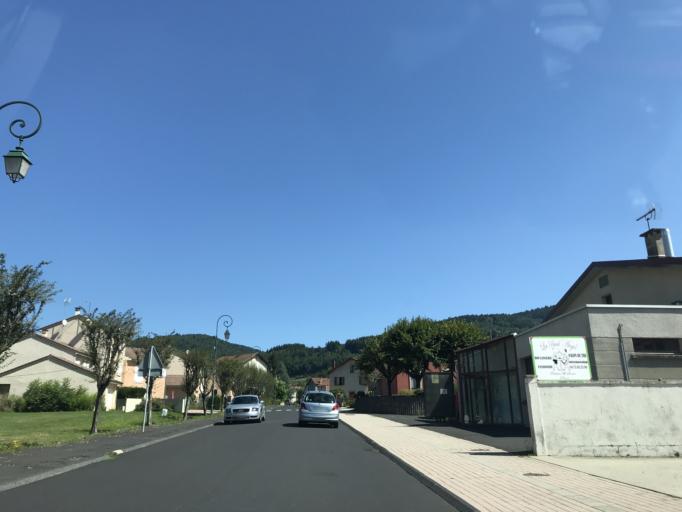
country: FR
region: Auvergne
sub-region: Departement du Puy-de-Dome
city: Job
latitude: 45.6487
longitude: 3.7088
